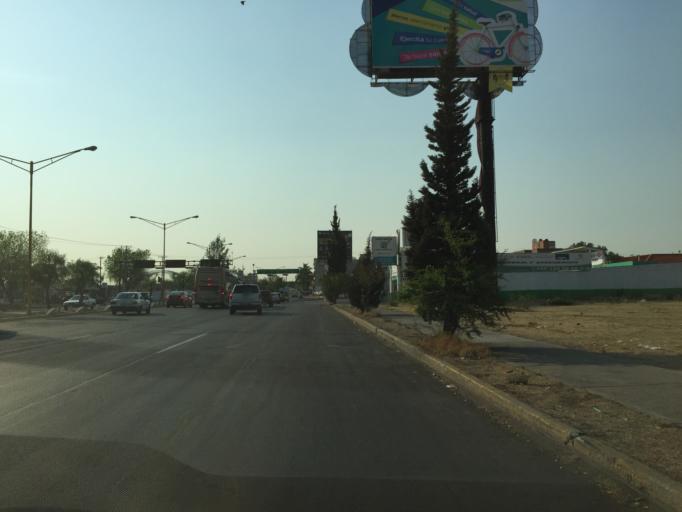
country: MX
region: Aguascalientes
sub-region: Aguascalientes
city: Aguascalientes
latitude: 21.8601
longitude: -102.3001
